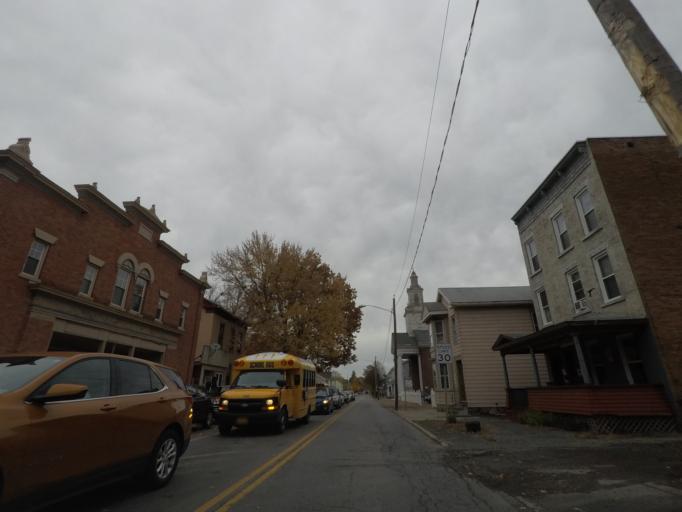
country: US
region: New York
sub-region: Saratoga County
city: Waterford
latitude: 42.7904
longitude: -73.6781
